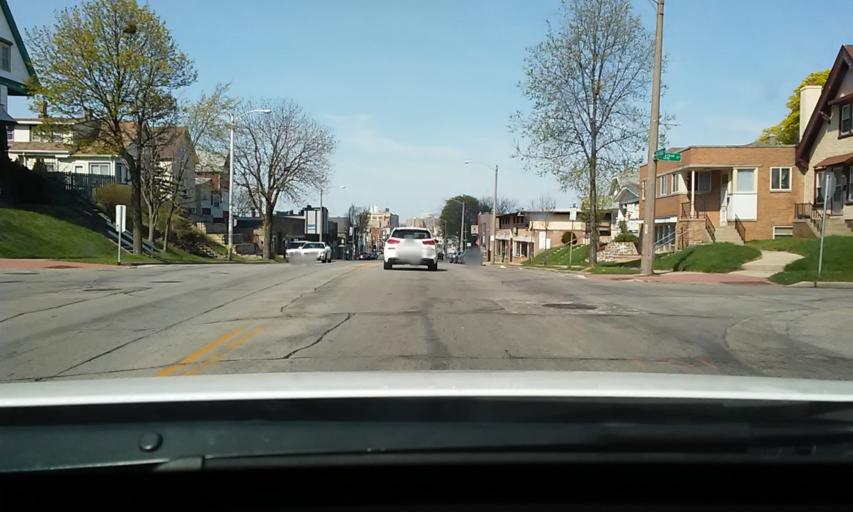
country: US
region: Wisconsin
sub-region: Milwaukee County
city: West Milwaukee
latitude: 43.0219
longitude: -87.9537
